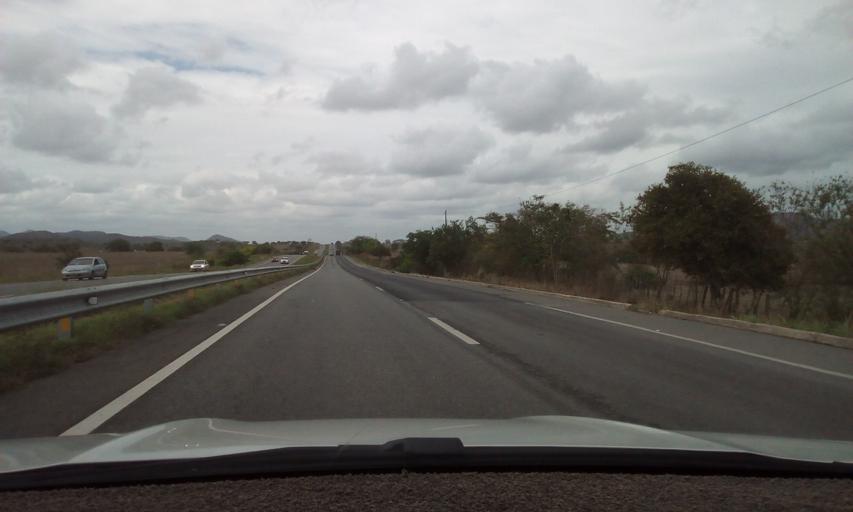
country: BR
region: Paraiba
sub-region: Gurinhem
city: Gurinhem
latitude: -7.1882
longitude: -35.4595
